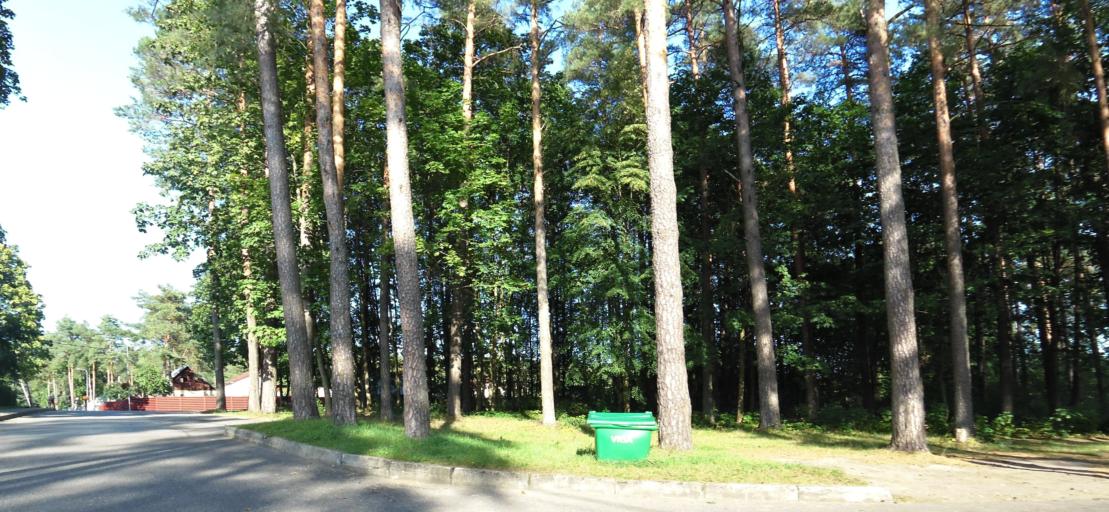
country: LT
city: Baltoji Voke
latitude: 54.5827
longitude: 25.2603
